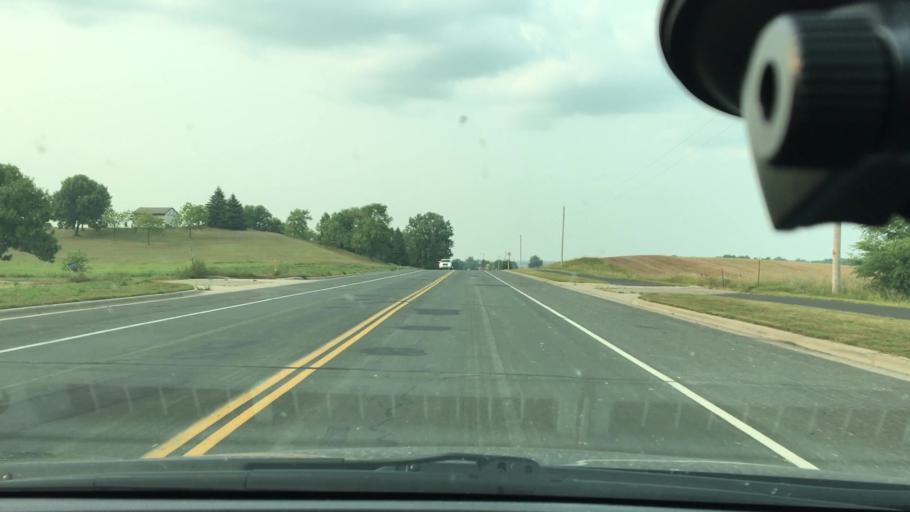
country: US
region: Minnesota
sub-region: Wright County
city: Otsego
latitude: 45.2593
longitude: -93.5606
